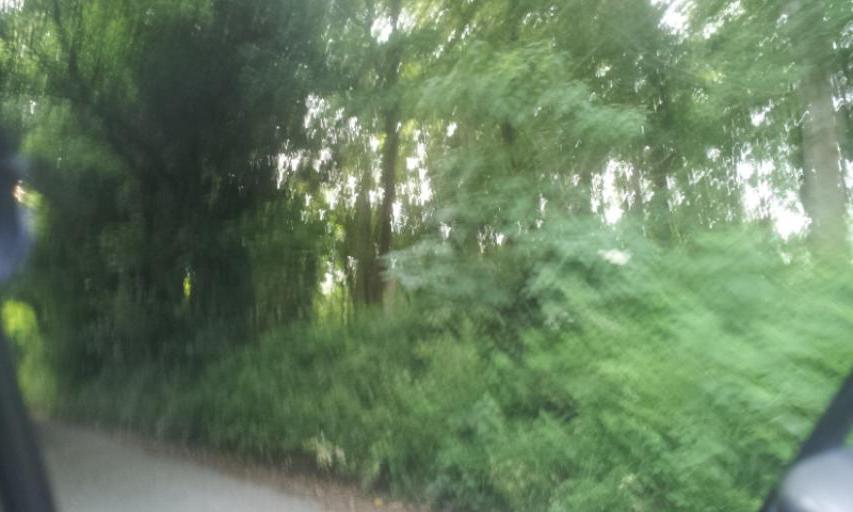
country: GB
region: England
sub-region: Kent
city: Lenham
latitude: 51.2484
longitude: 0.6962
